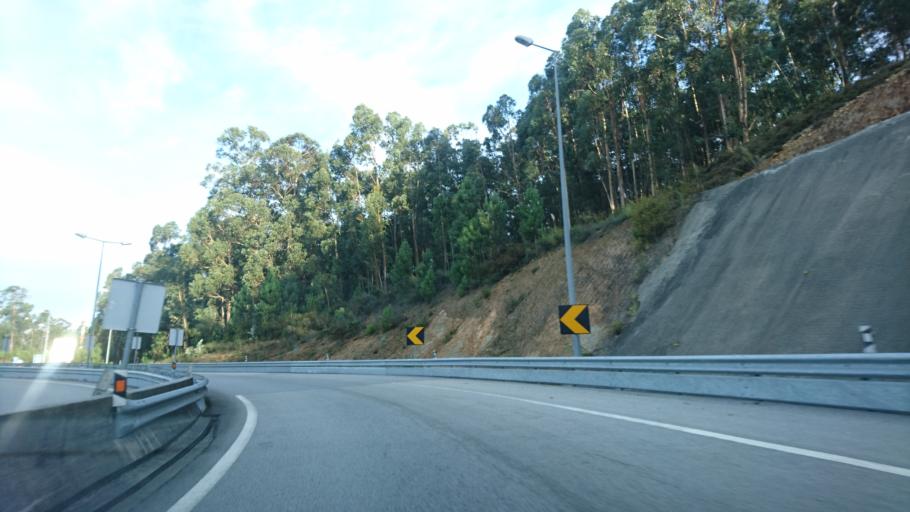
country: PT
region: Aveiro
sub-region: Santa Maria da Feira
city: Milheiros de Poiares
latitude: 40.9449
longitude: -8.4728
